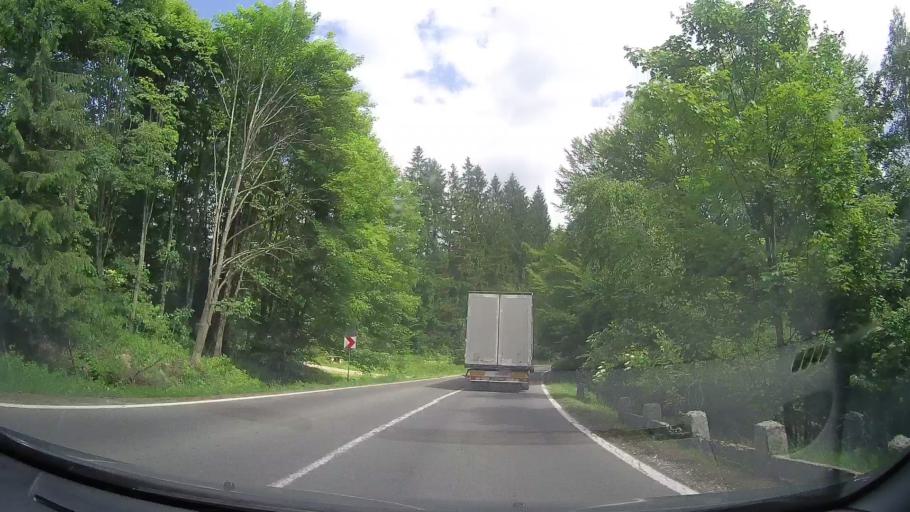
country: RO
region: Prahova
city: Maneciu
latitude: 45.3555
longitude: 25.9423
